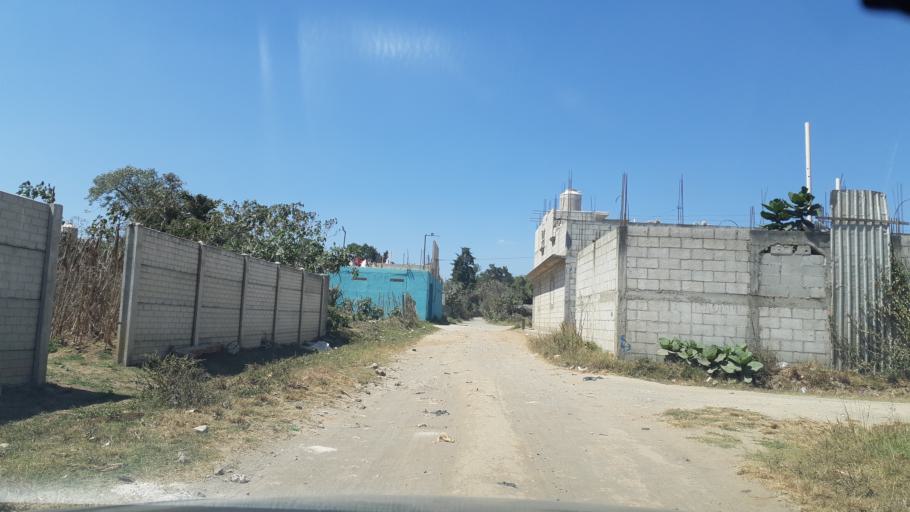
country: GT
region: Chimaltenango
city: El Tejar
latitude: 14.6475
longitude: -90.8096
